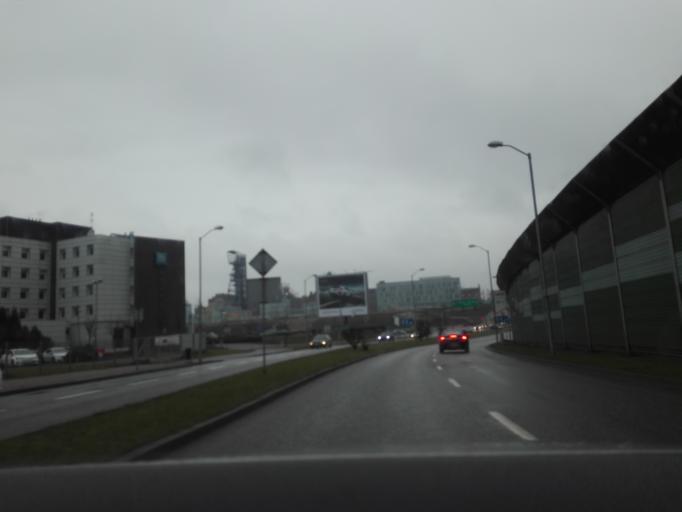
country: PL
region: Silesian Voivodeship
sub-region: Katowice
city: Katowice
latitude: 50.2605
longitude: 19.0353
